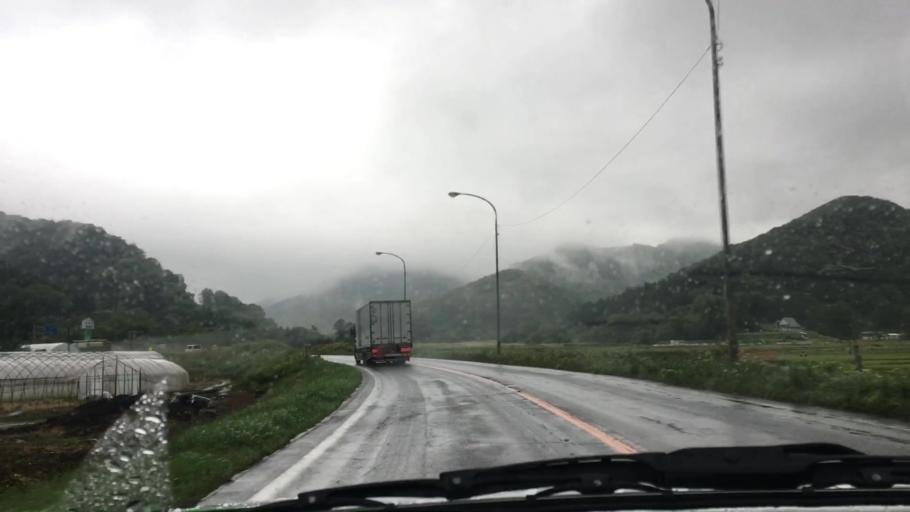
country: JP
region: Hokkaido
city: Niseko Town
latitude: 42.6008
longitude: 140.5875
